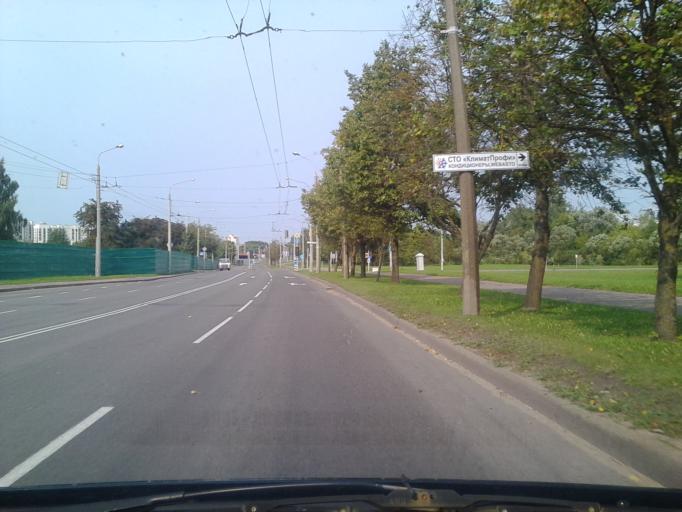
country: BY
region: Minsk
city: Syenitsa
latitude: 53.8643
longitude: 27.4968
